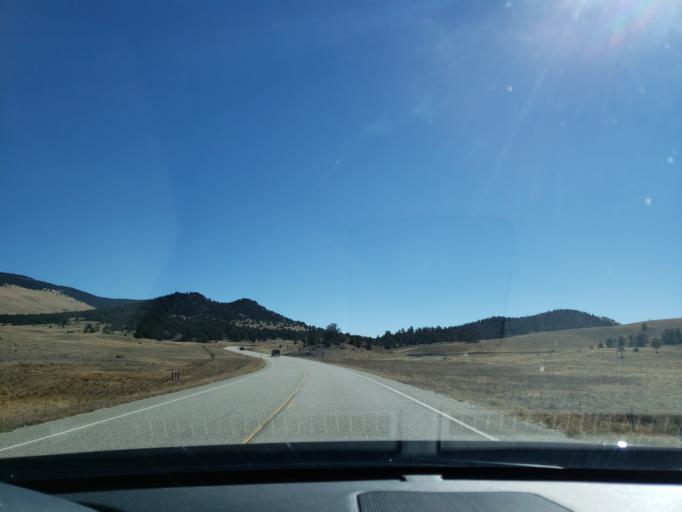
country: US
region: Colorado
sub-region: Chaffee County
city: Salida
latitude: 38.8492
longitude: -105.6494
